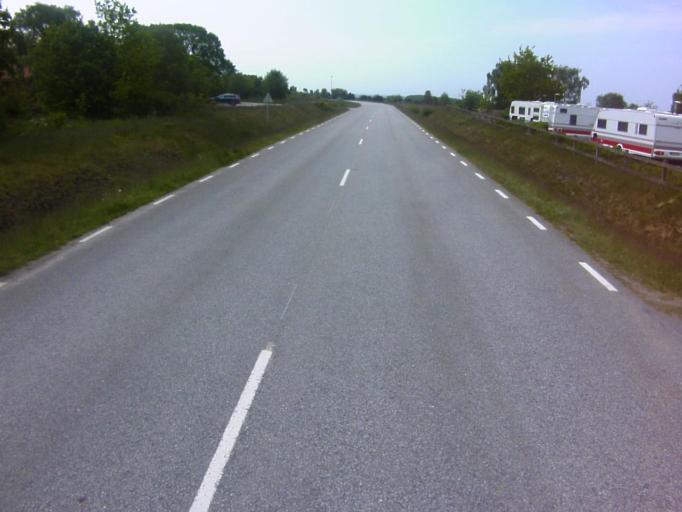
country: SE
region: Blekinge
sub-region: Solvesborgs Kommun
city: Soelvesborg
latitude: 56.0108
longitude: 14.7247
